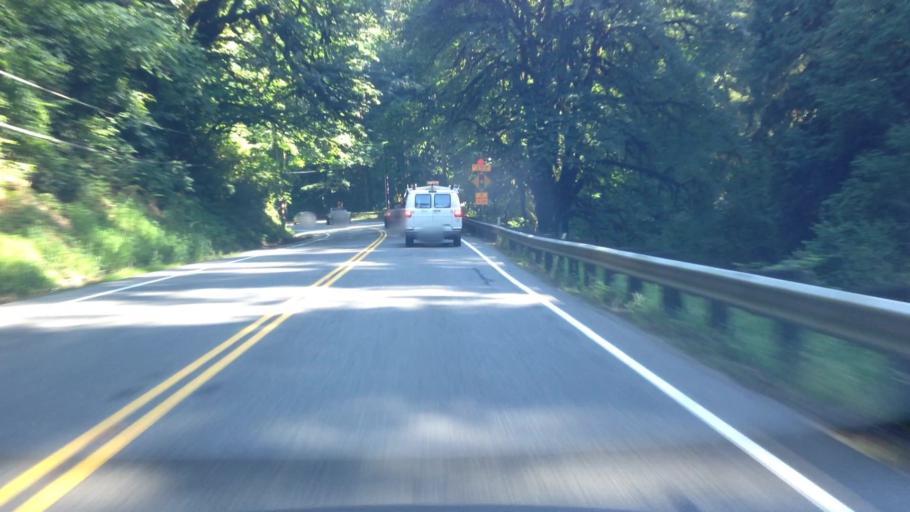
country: US
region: Washington
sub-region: King County
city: Duvall
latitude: 47.7462
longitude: -122.0139
